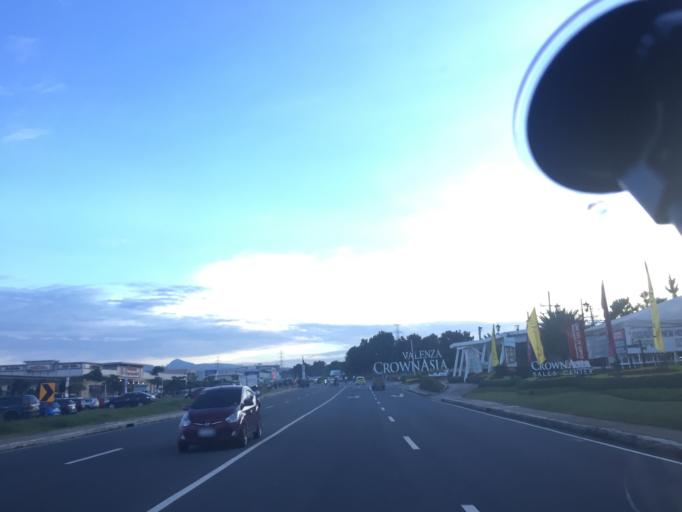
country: PH
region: Calabarzon
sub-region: Province of Cavite
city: Puting Kahoy
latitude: 14.2391
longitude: 121.0561
